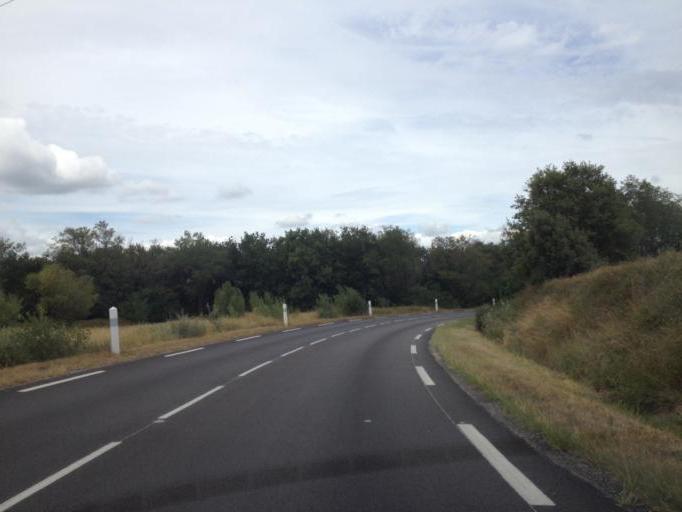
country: FR
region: Rhone-Alpes
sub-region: Departement de la Drome
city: Allan
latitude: 44.5264
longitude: 4.7664
